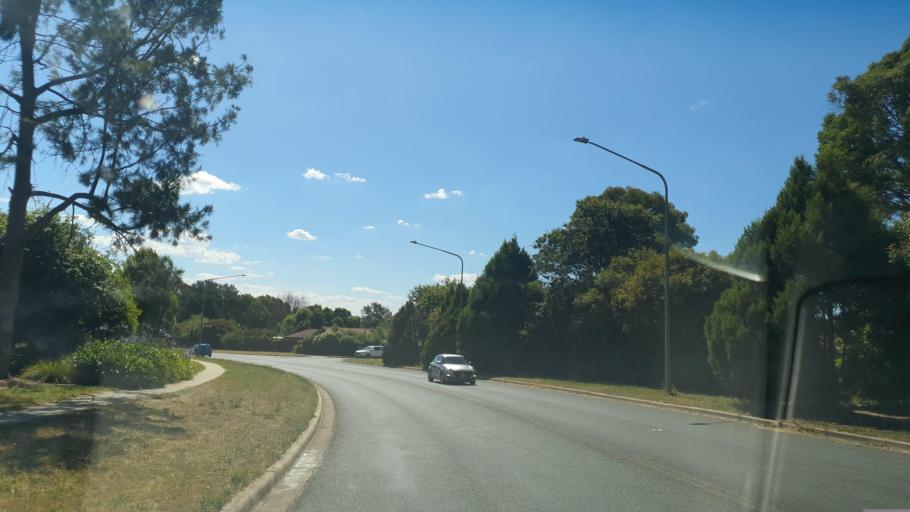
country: AU
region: Australian Capital Territory
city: Belconnen
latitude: -35.2259
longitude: 149.0600
